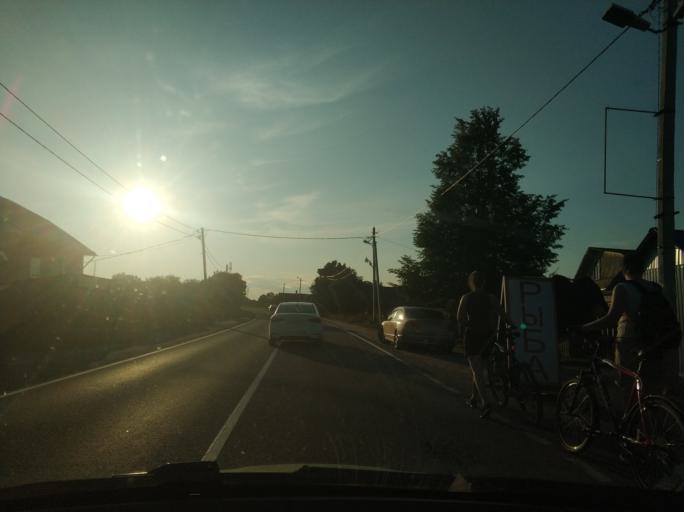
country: RU
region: Leningrad
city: Borisova Griva
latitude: 60.0844
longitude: 31.0292
